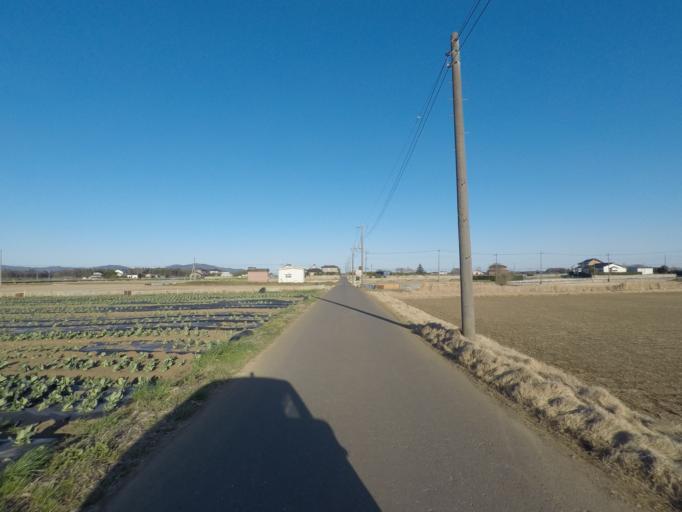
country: JP
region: Ibaraki
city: Ishige
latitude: 36.1345
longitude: 140.0123
